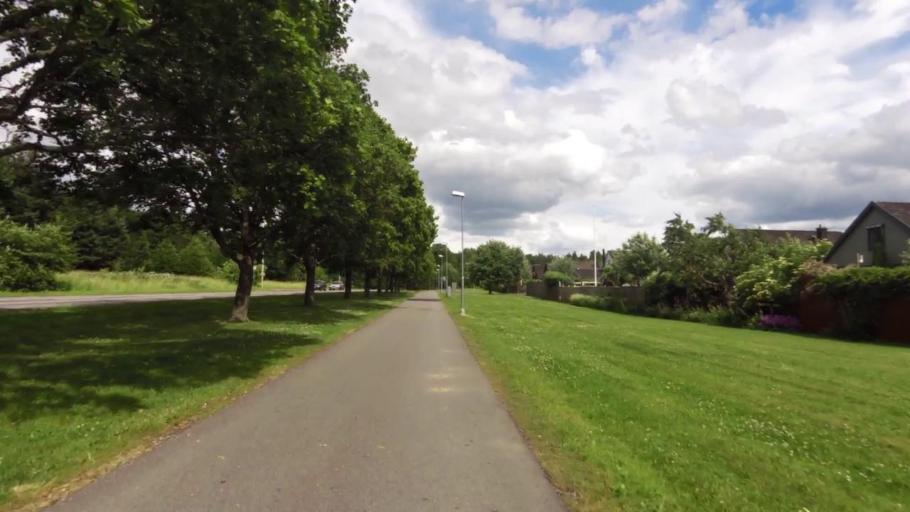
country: SE
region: OEstergoetland
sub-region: Linkopings Kommun
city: Malmslatt
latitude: 58.4191
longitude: 15.5612
